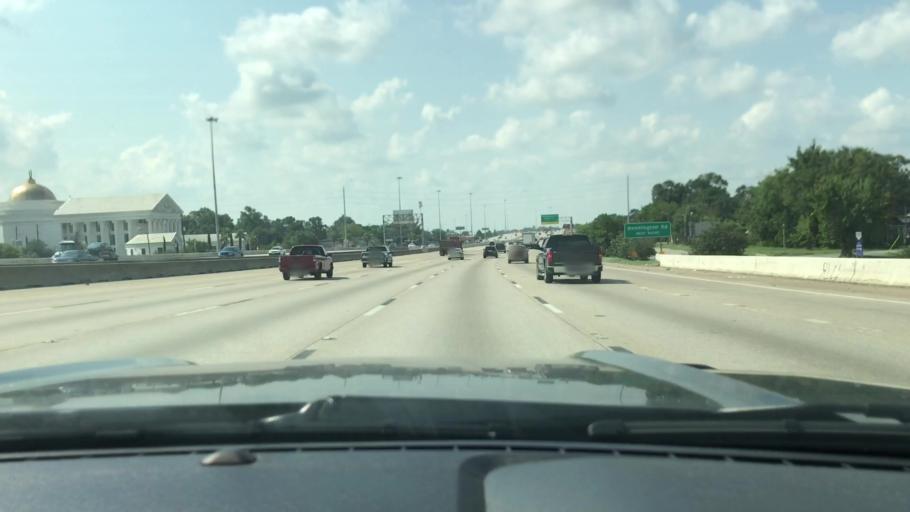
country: US
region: Texas
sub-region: Harris County
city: Houston
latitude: 29.8384
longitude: -95.3337
